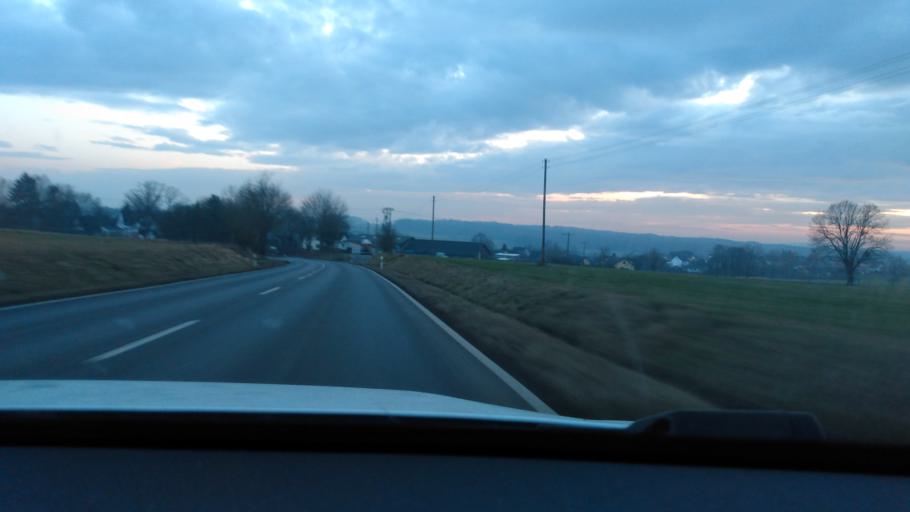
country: DE
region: Rheinland-Pfalz
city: Kircheib
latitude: 50.7031
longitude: 7.4354
